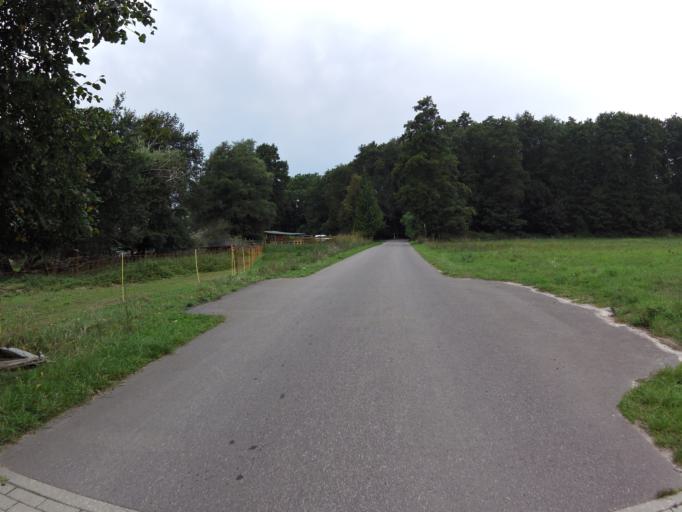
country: DE
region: Mecklenburg-Vorpommern
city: Seebad Heringsdorf
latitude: 53.9294
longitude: 14.1496
